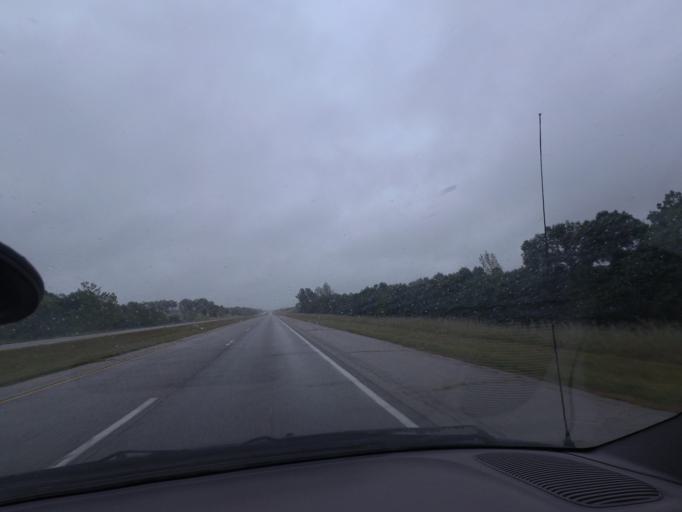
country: US
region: Illinois
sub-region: Pike County
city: Barry
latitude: 39.6910
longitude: -90.9305
